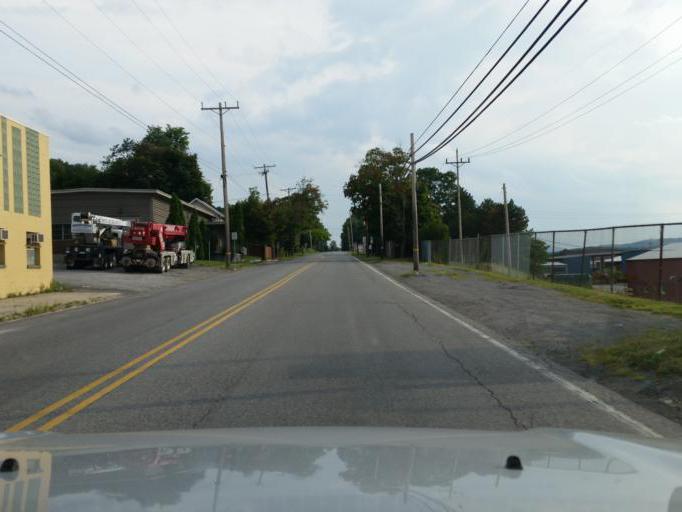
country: US
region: Pennsylvania
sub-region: Blair County
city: Lakemont
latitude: 40.4841
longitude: -78.4169
